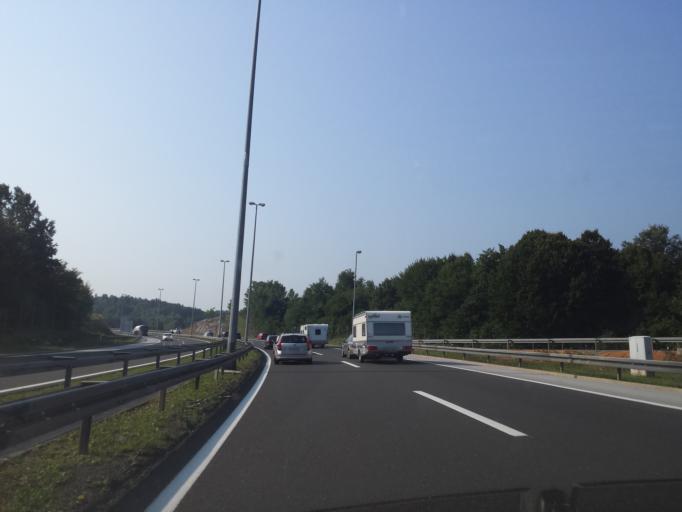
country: HR
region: Karlovacka
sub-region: Grad Ogulin
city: Ogulin
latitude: 45.4040
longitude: 15.2492
